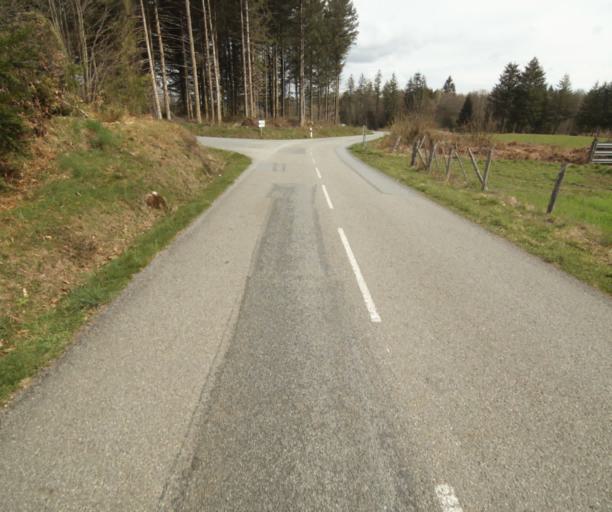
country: FR
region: Limousin
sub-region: Departement de la Correze
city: Correze
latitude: 45.3843
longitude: 1.9229
